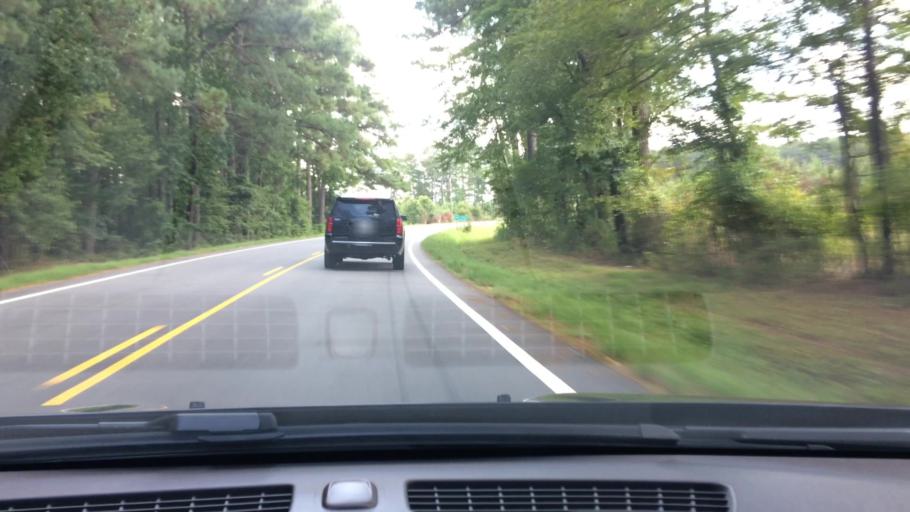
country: US
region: North Carolina
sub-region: Craven County
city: Vanceboro
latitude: 35.4289
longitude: -77.2053
